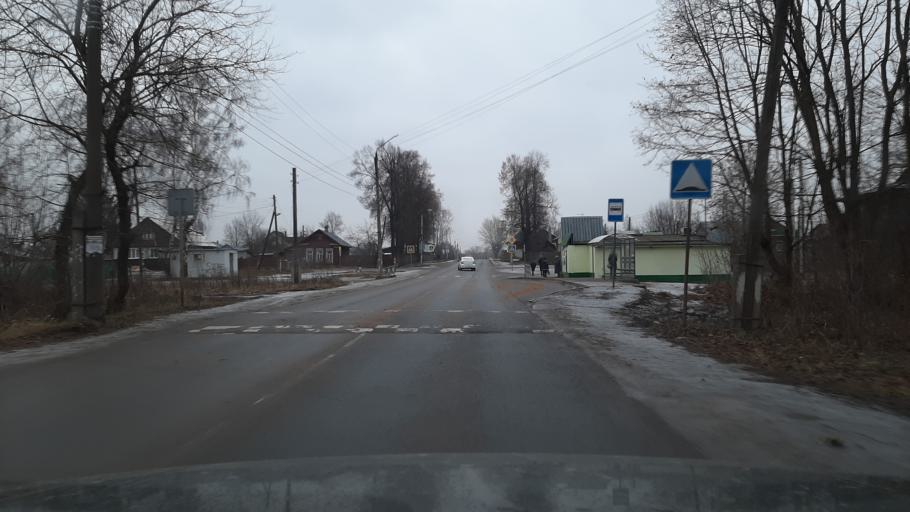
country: RU
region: Ivanovo
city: Shuya
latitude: 56.8631
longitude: 41.3648
